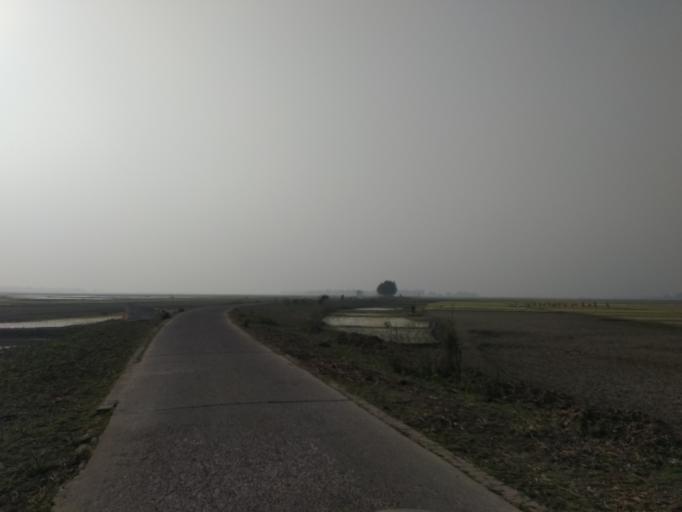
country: BD
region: Rajshahi
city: Ishurdi
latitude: 24.4838
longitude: 89.2204
